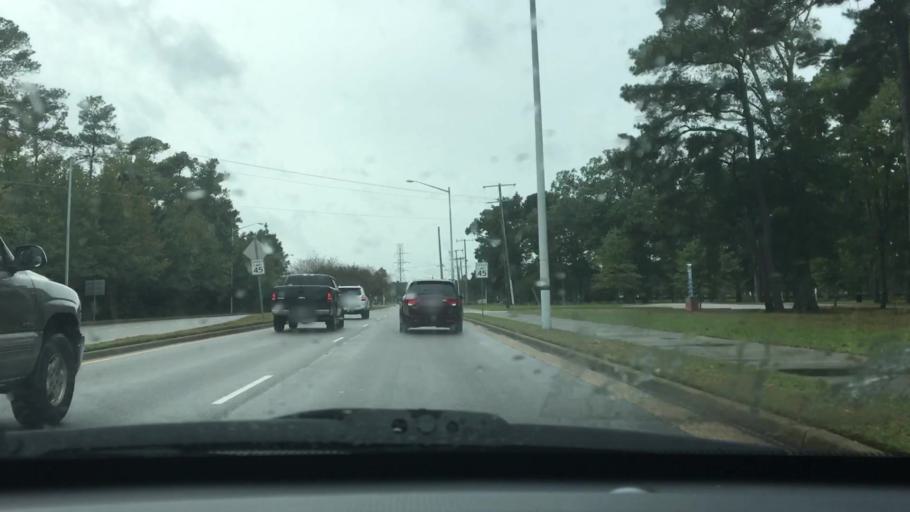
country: US
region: Virginia
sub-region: City of Virginia Beach
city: Virginia Beach
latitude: 36.7752
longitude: -76.0924
